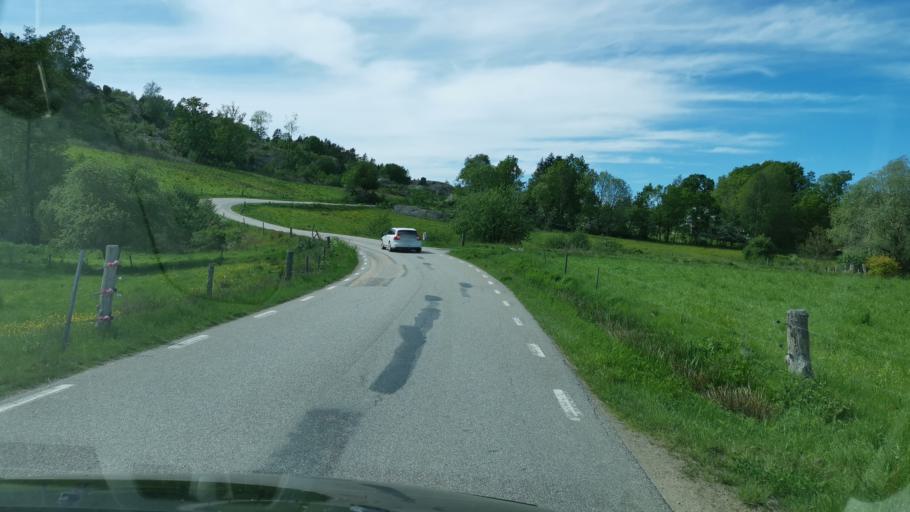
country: SE
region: Vaestra Goetaland
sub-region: Orust
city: Henan
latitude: 58.2706
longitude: 11.6029
